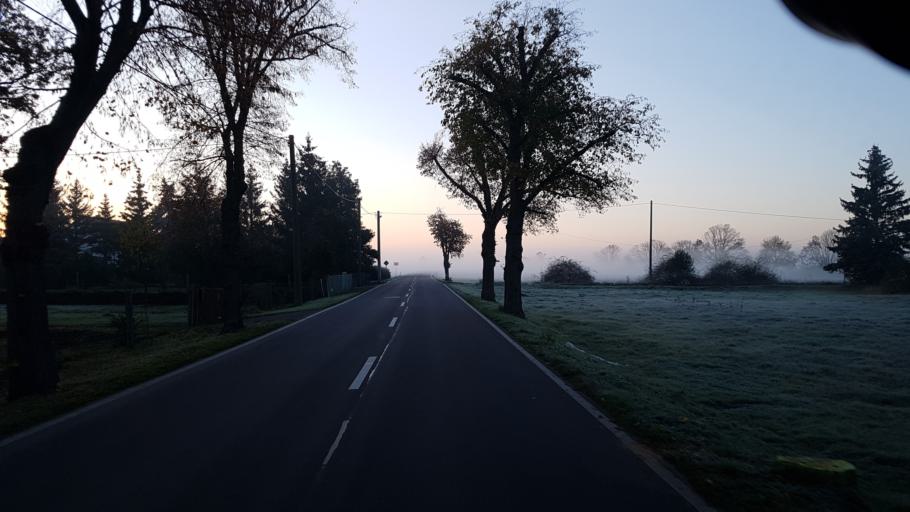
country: DE
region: Saxony
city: Arzberg
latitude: 51.5405
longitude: 13.1700
